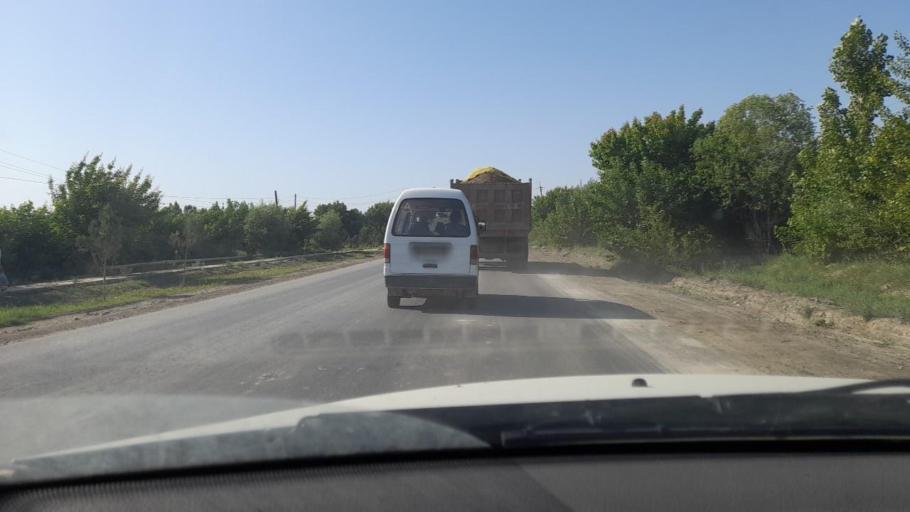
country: UZ
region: Bukhara
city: Romiton
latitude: 40.0510
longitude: 64.3284
